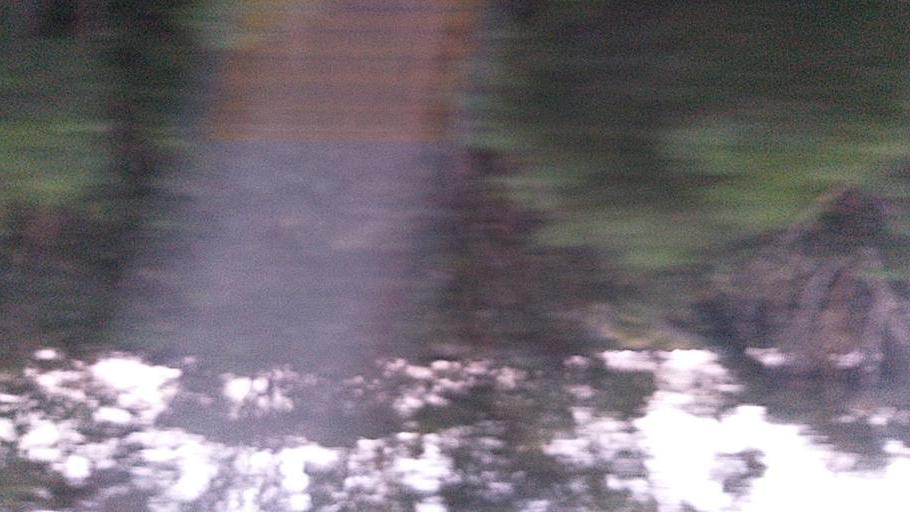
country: AU
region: New South Wales
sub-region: Wollongong
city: Helensburgh
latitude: -34.1632
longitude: 151.0015
